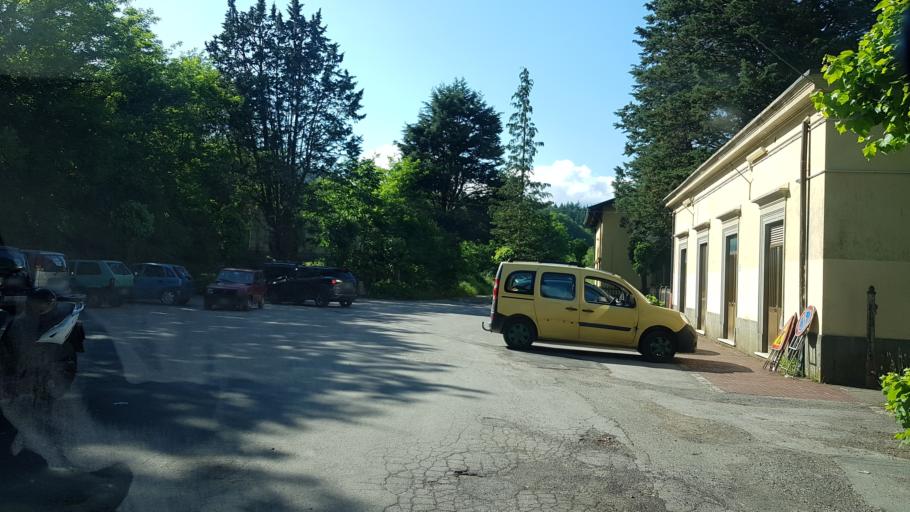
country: IT
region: Tuscany
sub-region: Provincia di Lucca
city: Camporgiano
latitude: 44.1611
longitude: 10.3347
